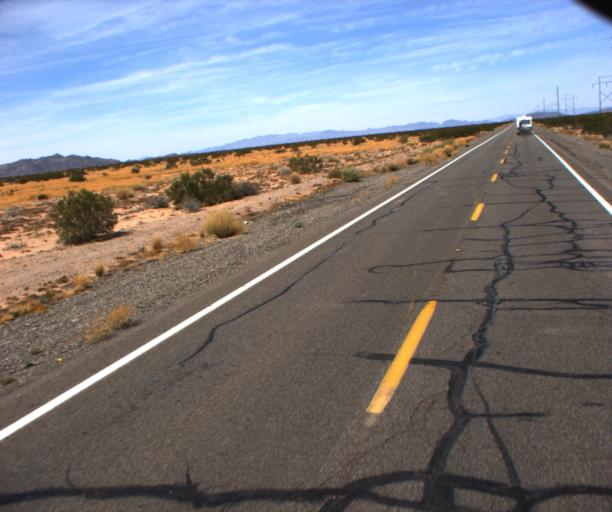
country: US
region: Arizona
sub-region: La Paz County
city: Parker
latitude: 33.9287
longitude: -114.2169
